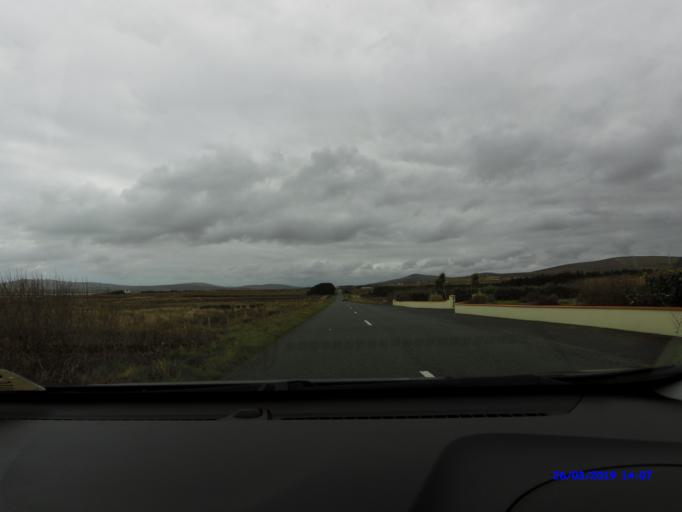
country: IE
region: Connaught
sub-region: Maigh Eo
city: Belmullet
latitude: 54.2076
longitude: -9.9184
